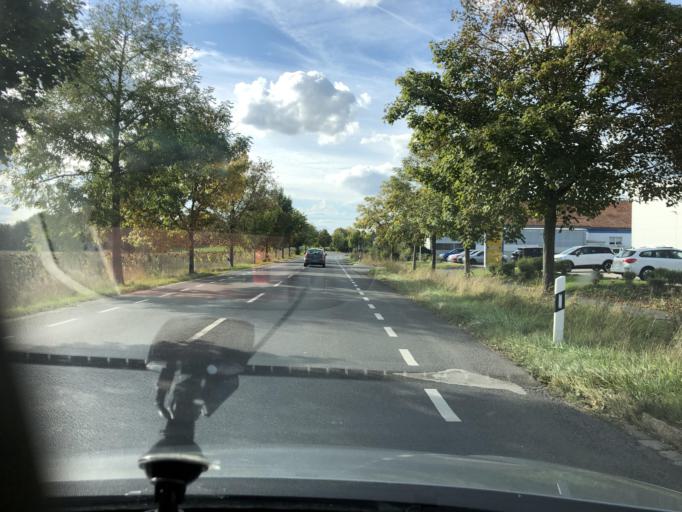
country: DE
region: Bavaria
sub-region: Regierungsbezirk Mittelfranken
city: Langenzenn
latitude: 49.4944
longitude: 10.8165
